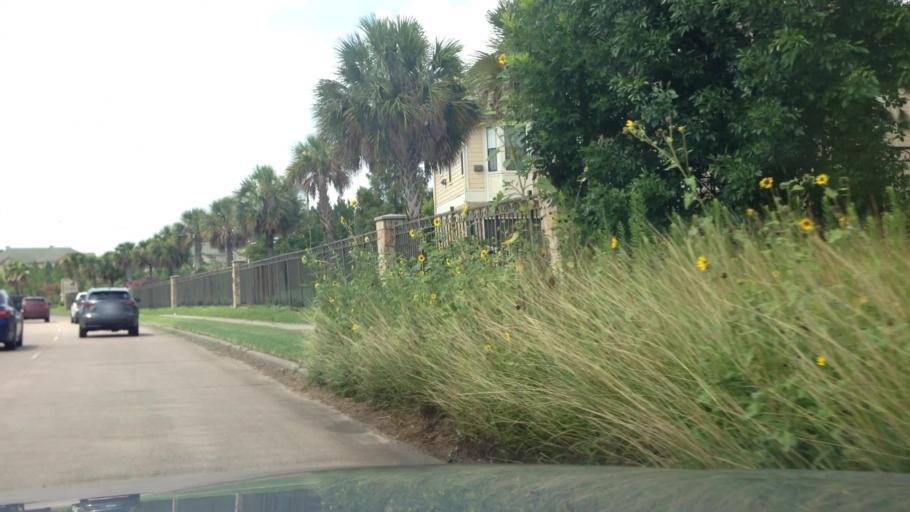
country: US
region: Texas
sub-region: Harris County
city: Jersey Village
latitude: 29.9526
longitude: -95.5472
